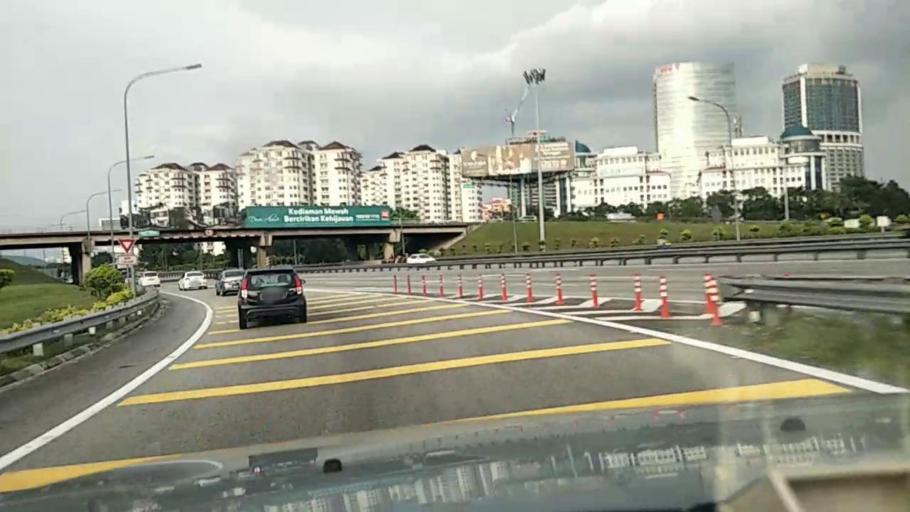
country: MY
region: Selangor
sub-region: Petaling
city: Petaling Jaya
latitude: 3.1058
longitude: 101.5892
